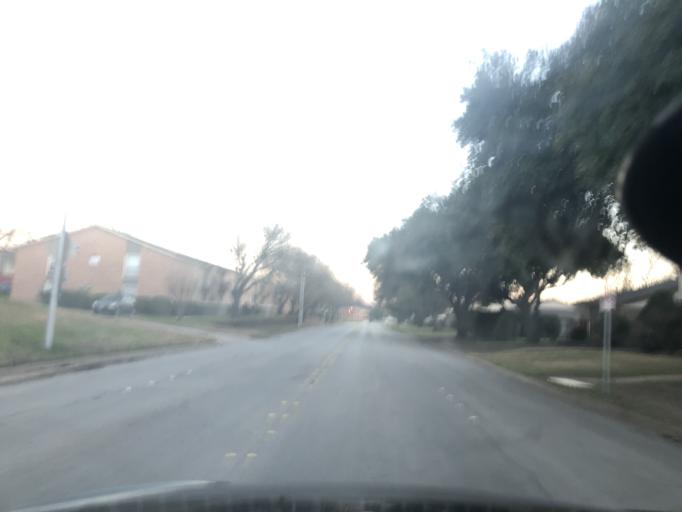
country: US
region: Texas
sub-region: Tarrant County
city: White Settlement
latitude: 32.7318
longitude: -97.4702
